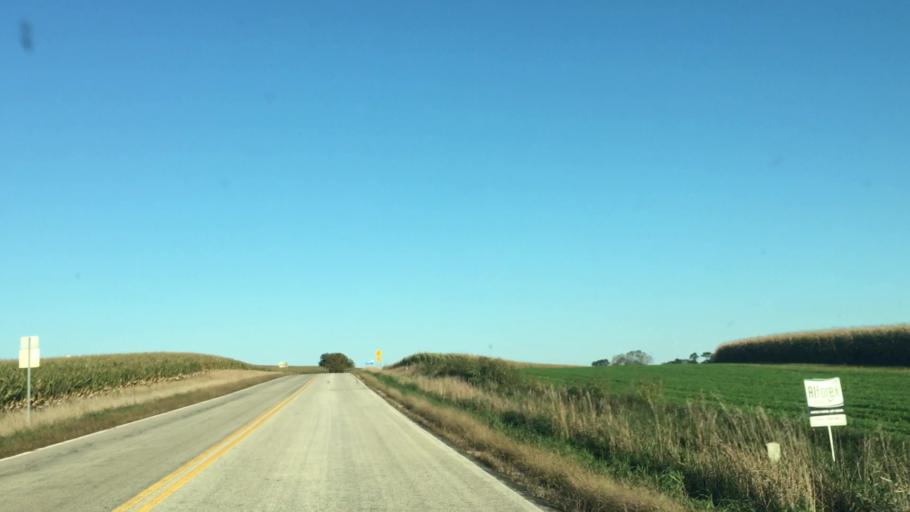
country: US
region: Minnesota
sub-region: Fillmore County
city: Chatfield
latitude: 43.8183
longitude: -92.0643
